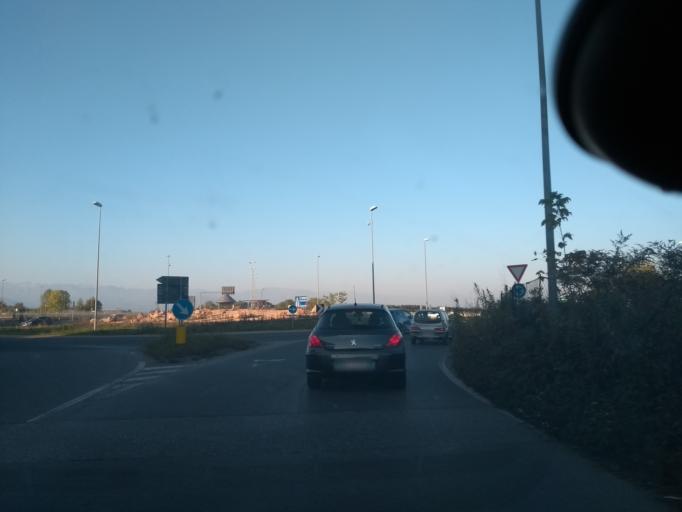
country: IT
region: Piedmont
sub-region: Provincia di Torino
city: Collegno
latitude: 45.0798
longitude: 7.5877
